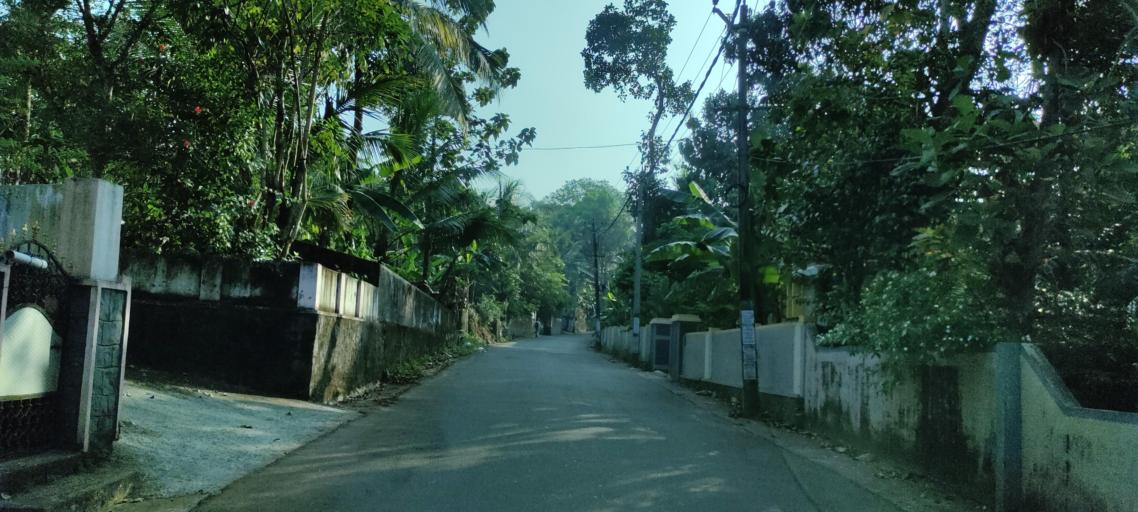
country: IN
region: Kerala
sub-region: Pattanamtitta
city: Adur
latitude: 9.1487
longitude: 76.7488
